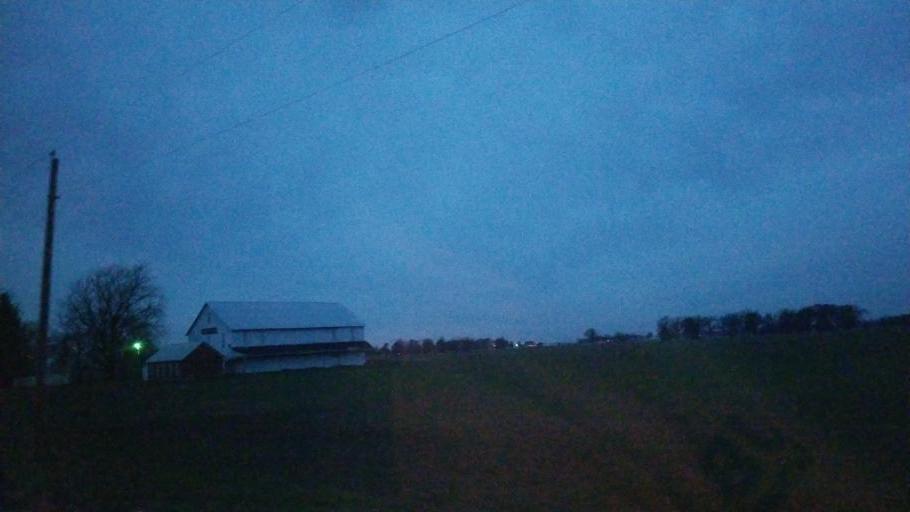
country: US
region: Indiana
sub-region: Adams County
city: Berne
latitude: 40.6938
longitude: -84.9753
